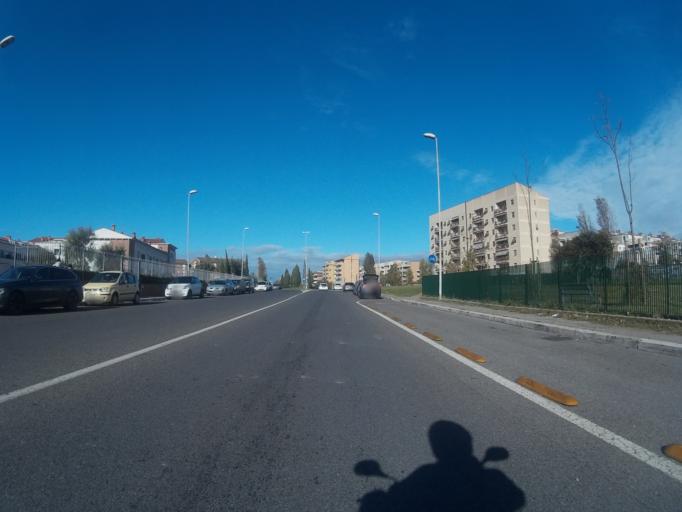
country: IT
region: Tuscany
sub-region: Provincia di Livorno
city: Livorno
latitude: 43.5253
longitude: 10.3456
